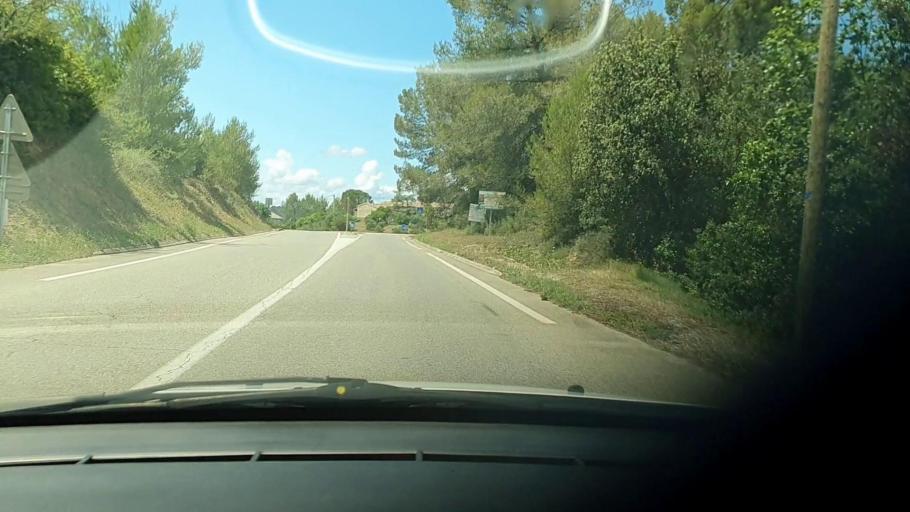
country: FR
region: Languedoc-Roussillon
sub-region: Departement du Gard
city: Mons
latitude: 44.0703
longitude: 4.2245
